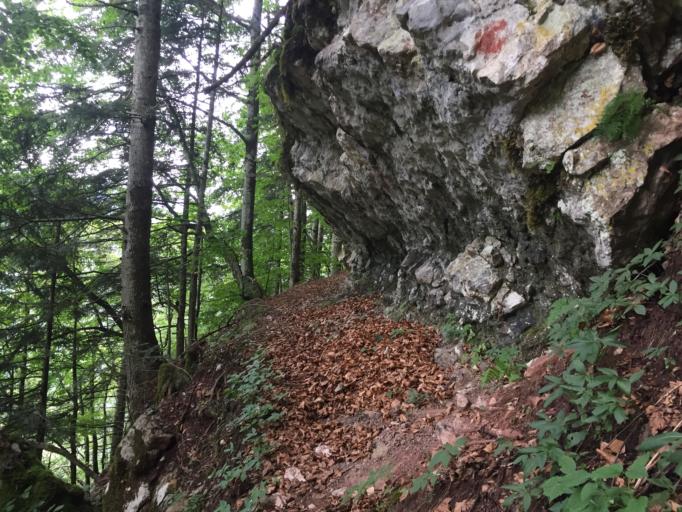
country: IT
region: Friuli Venezia Giulia
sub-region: Provincia di Udine
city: Forni Avoltri
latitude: 46.5778
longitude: 12.7833
